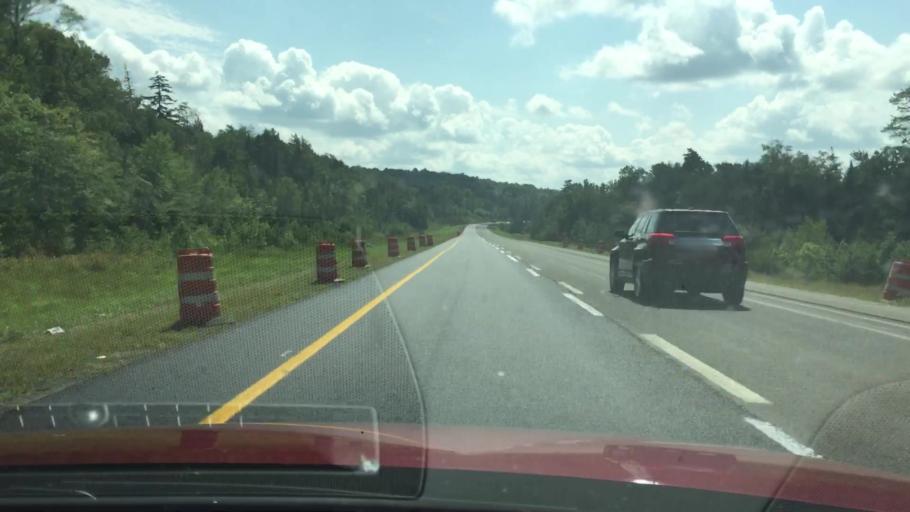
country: US
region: Maine
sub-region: Penobscot County
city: Medway
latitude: 45.7172
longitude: -68.4756
